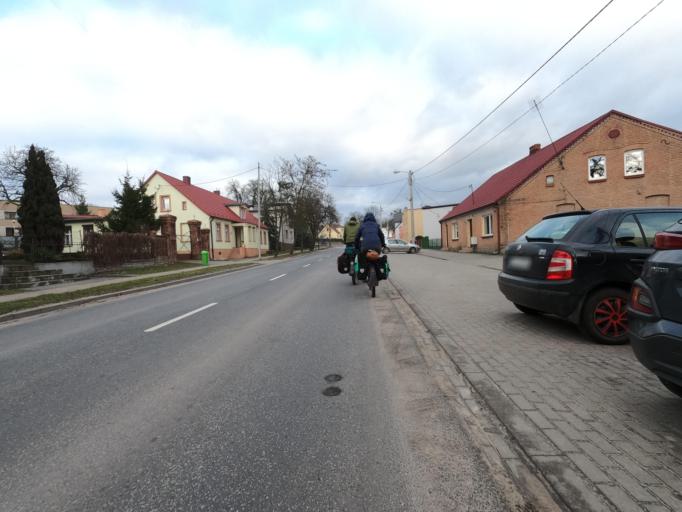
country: PL
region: Greater Poland Voivodeship
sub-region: Powiat pilski
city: Bialosliwie
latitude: 53.0991
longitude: 17.1213
